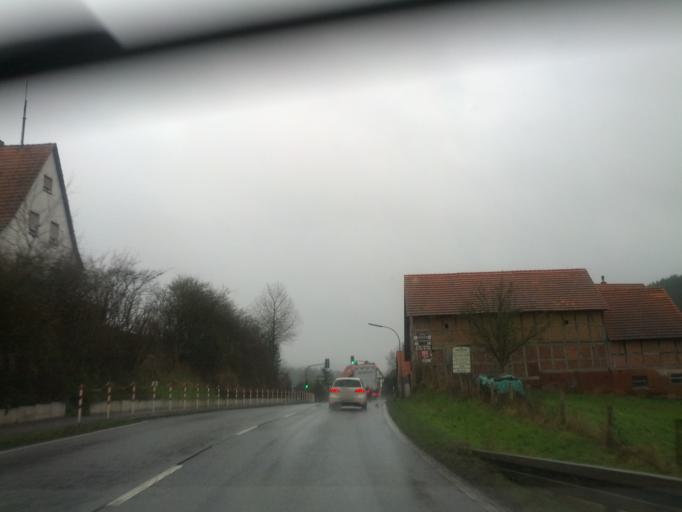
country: DE
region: Hesse
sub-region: Regierungsbezirk Kassel
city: Sontra
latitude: 51.0888
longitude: 9.9778
